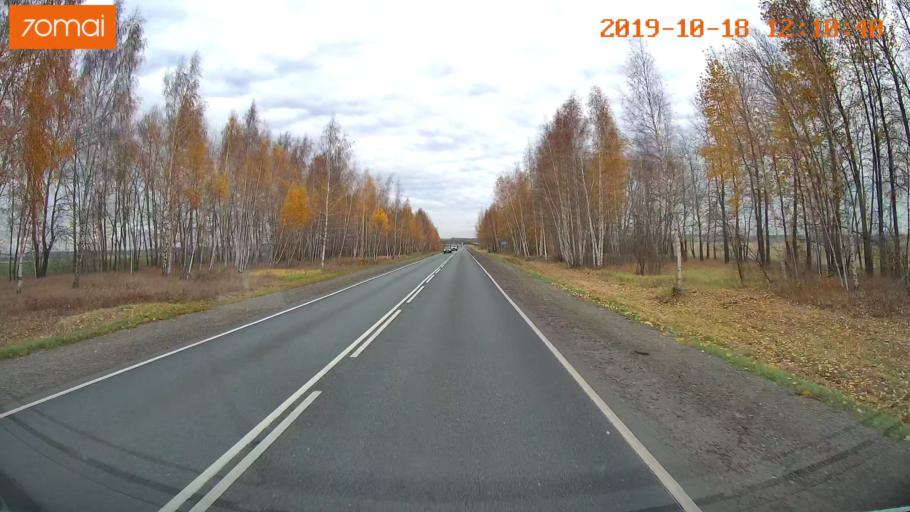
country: RU
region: Rjazan
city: Zakharovo
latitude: 54.3943
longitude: 39.3358
